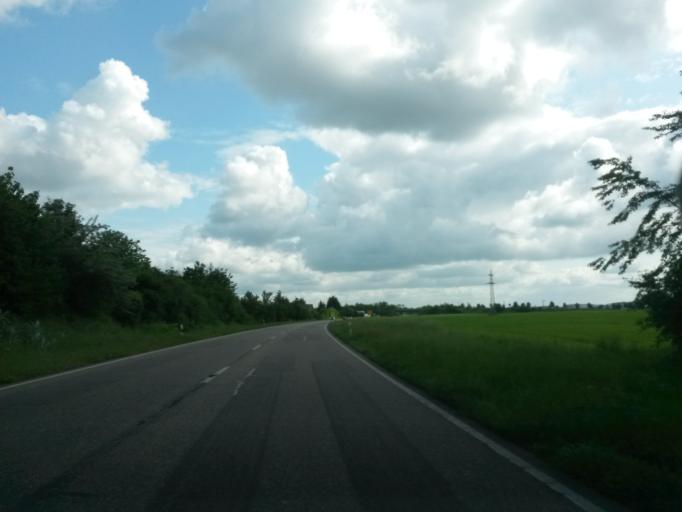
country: DE
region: Baden-Wuerttemberg
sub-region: Karlsruhe Region
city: Eggenstein-Leopoldshafen
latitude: 49.0721
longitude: 8.4561
